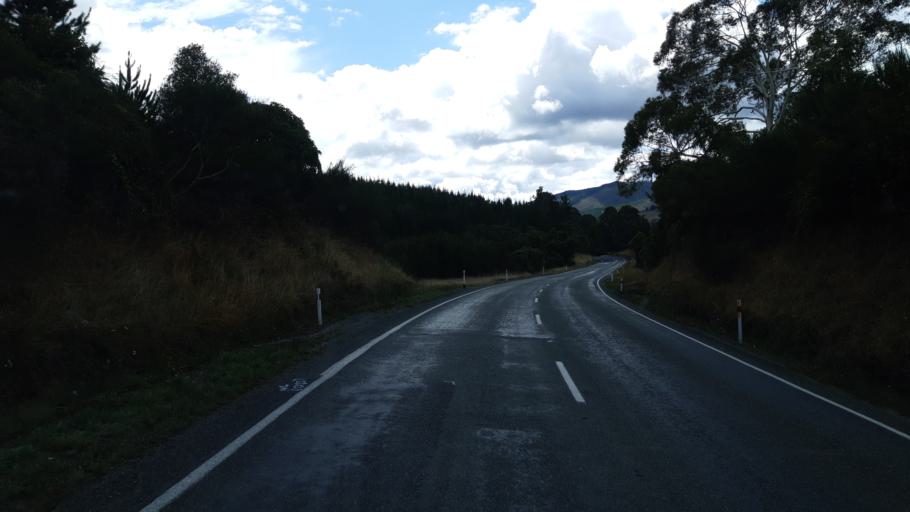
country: NZ
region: Tasman
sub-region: Tasman District
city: Wakefield
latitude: -41.5517
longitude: 172.7901
